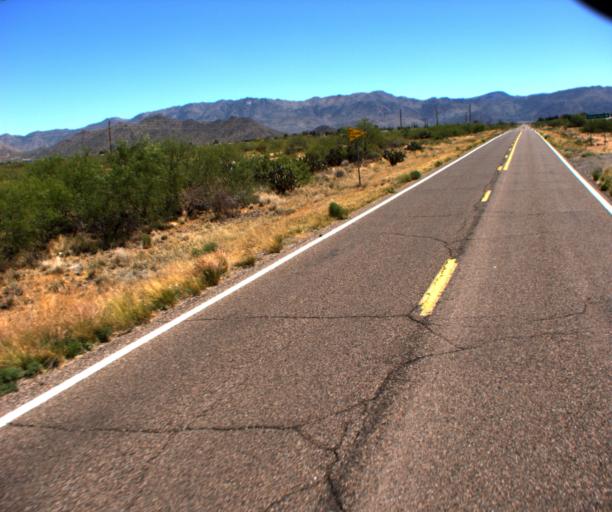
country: US
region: Arizona
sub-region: Yavapai County
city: Congress
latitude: 34.1570
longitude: -112.8659
